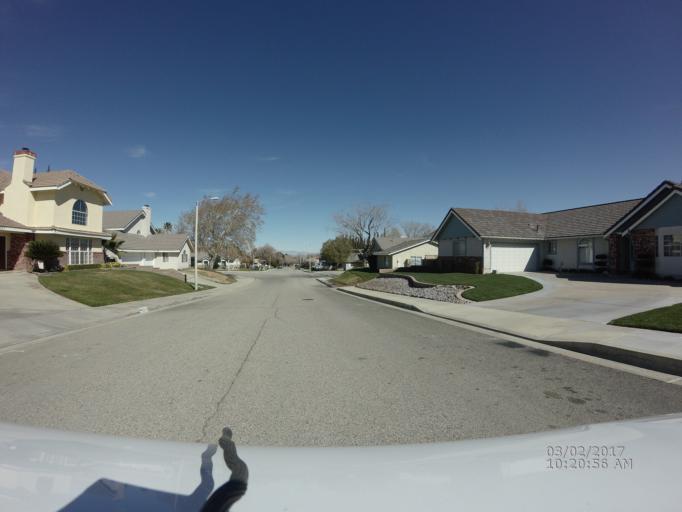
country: US
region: California
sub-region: Los Angeles County
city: Quartz Hill
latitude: 34.6396
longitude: -118.2344
